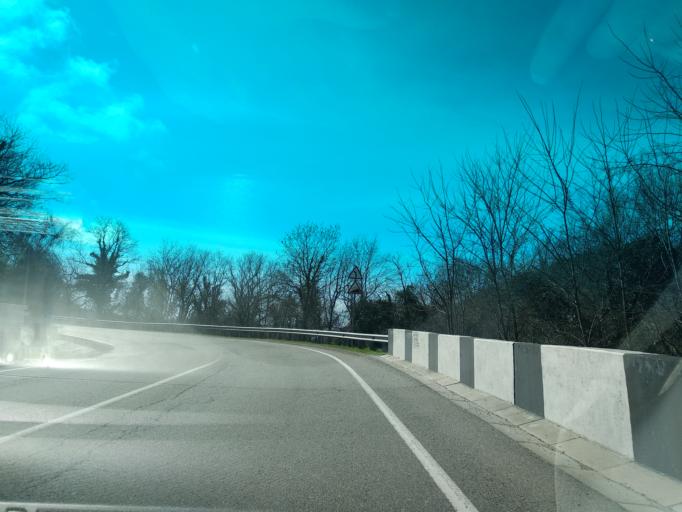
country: RU
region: Krasnodarskiy
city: Tuapse
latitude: 44.0908
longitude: 39.1184
